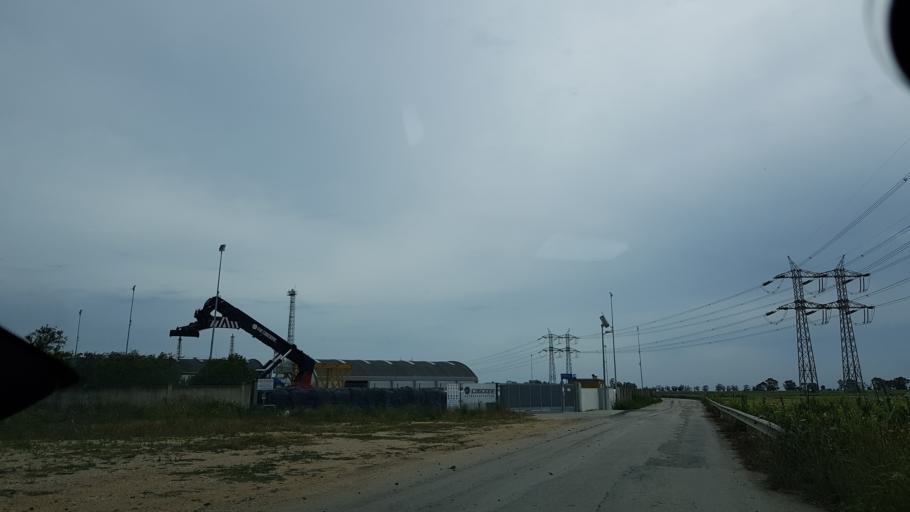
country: IT
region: Apulia
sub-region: Provincia di Brindisi
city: La Rosa
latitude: 40.6239
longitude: 17.9902
